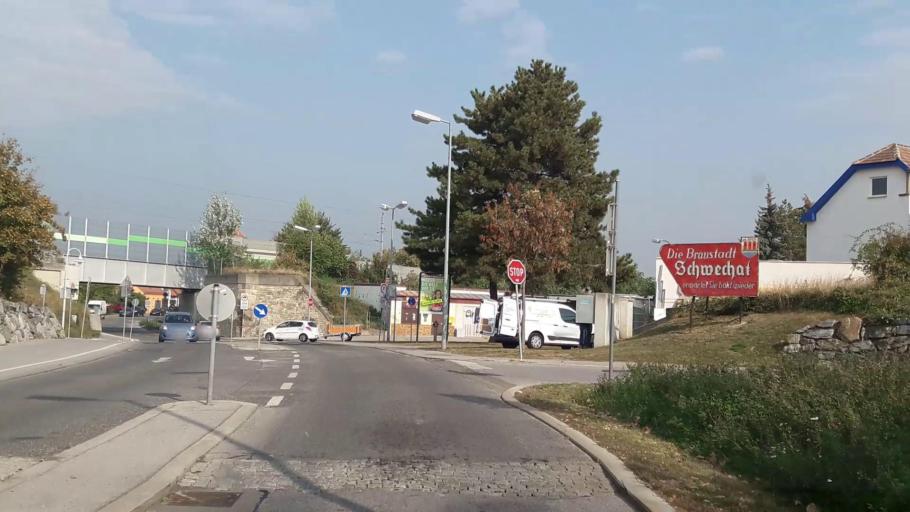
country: AT
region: Lower Austria
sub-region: Politischer Bezirk Wien-Umgebung
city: Schwechat
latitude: 48.1492
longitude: 16.4711
